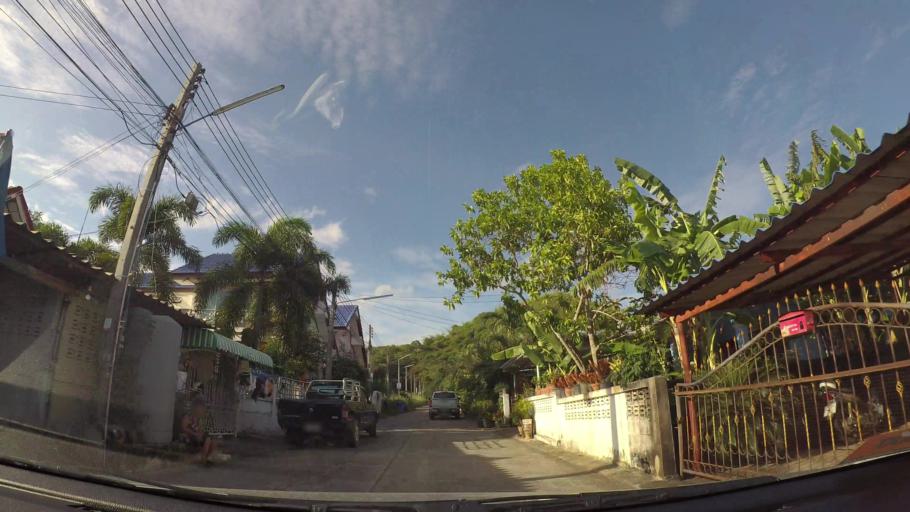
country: TH
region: Chon Buri
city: Sattahip
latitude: 12.6760
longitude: 100.9162
